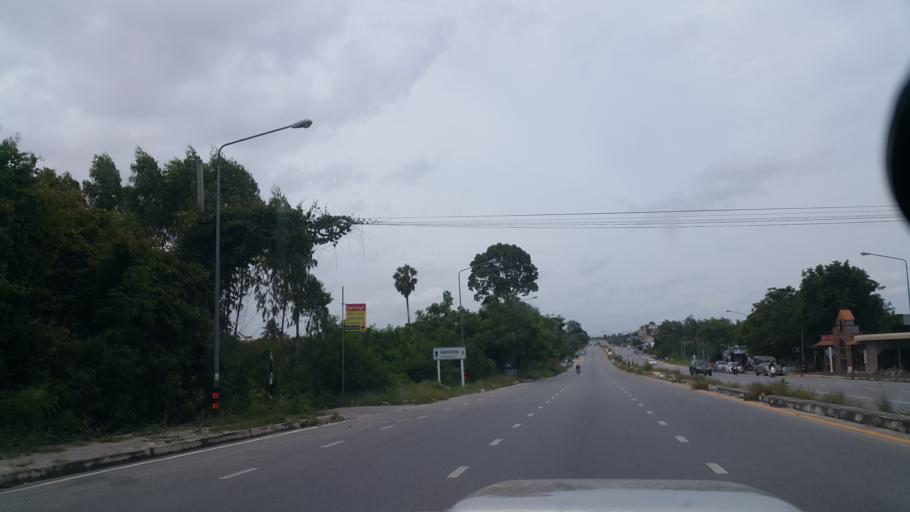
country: TH
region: Rayong
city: Ban Chang
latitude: 12.7148
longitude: 101.0586
